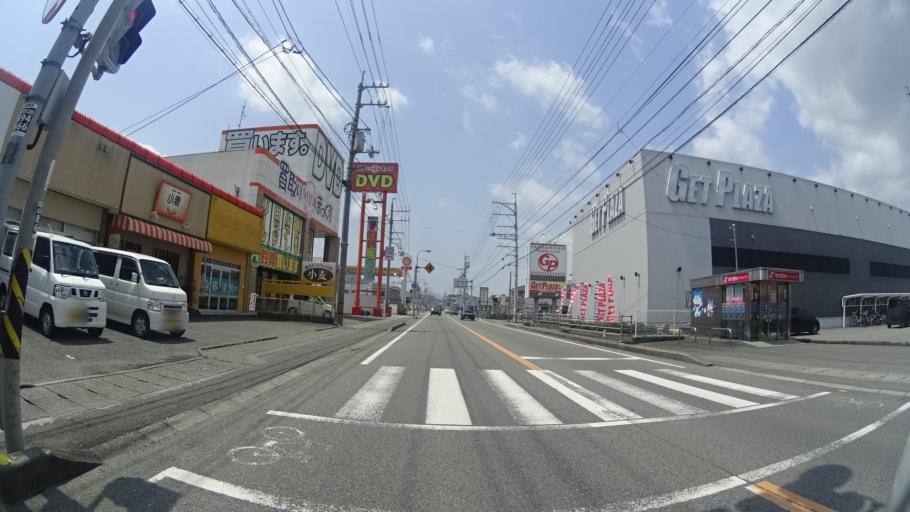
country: JP
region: Tokushima
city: Ishii
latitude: 34.0693
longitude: 134.4508
